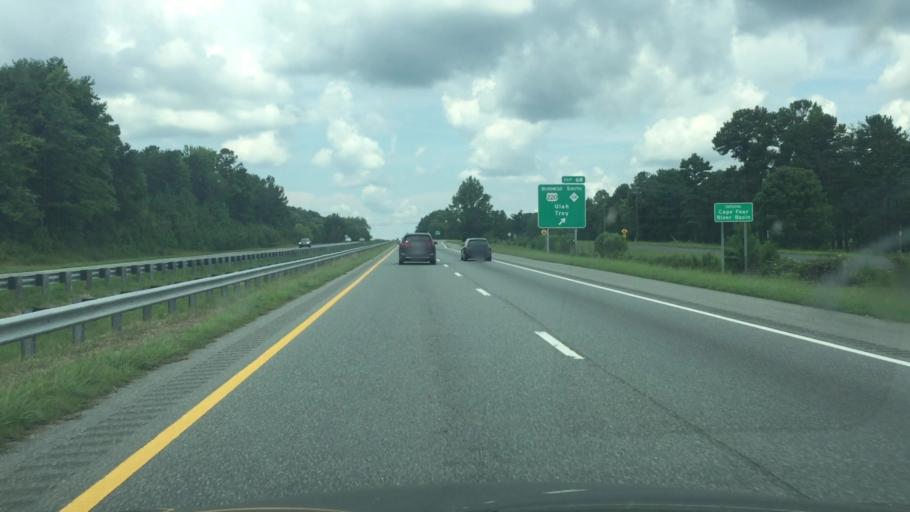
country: US
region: North Carolina
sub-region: Randolph County
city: Asheboro
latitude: 35.6163
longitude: -79.8222
